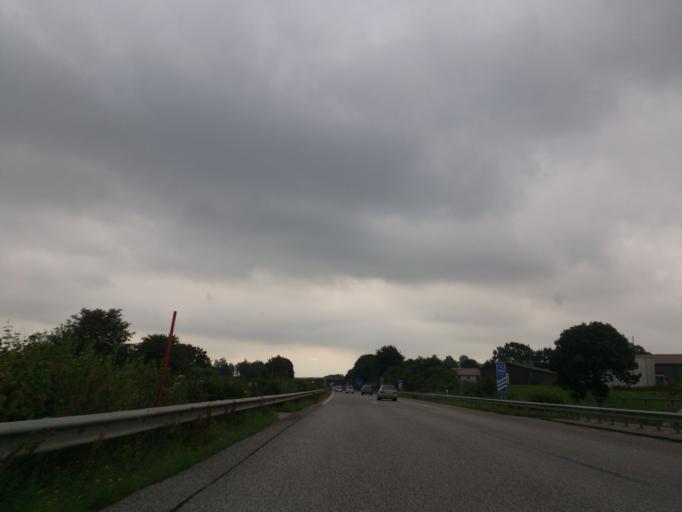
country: DE
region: Schleswig-Holstein
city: Rethwisch
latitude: 53.8463
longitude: 9.5935
